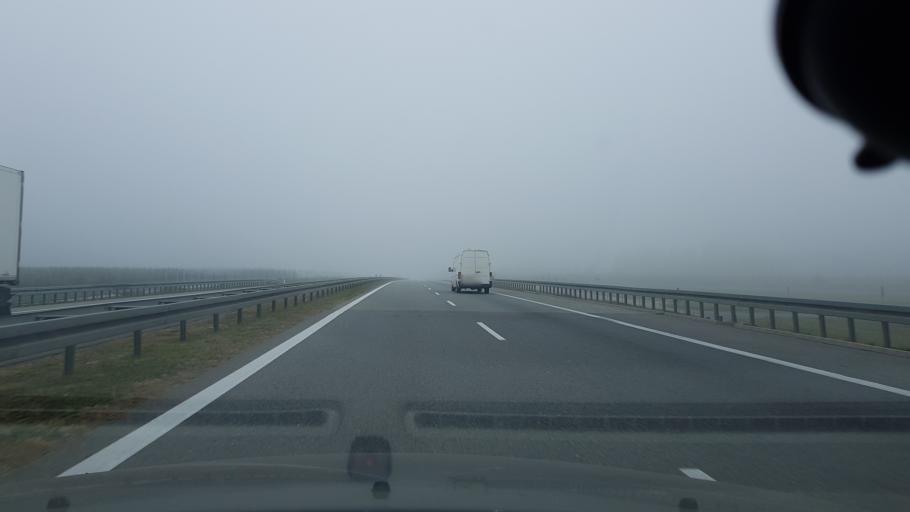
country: PL
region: Lodz Voivodeship
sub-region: Powiat skierniewicki
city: Kowiesy
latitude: 51.9119
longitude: 20.4465
